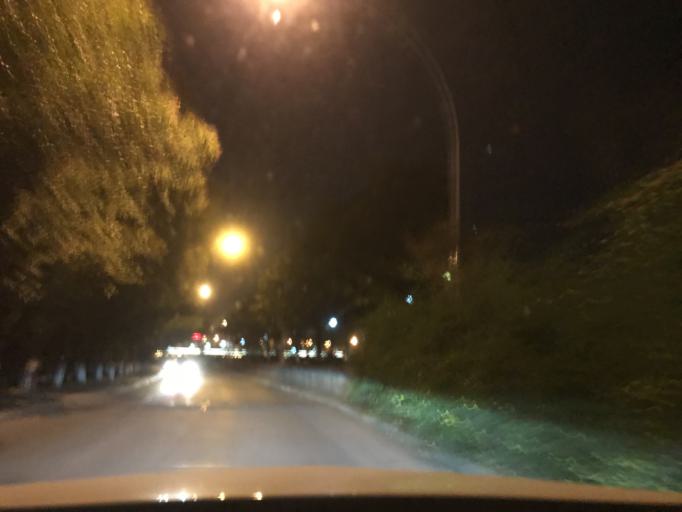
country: CN
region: Sichuan
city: Mianyang
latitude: 31.4497
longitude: 104.7486
